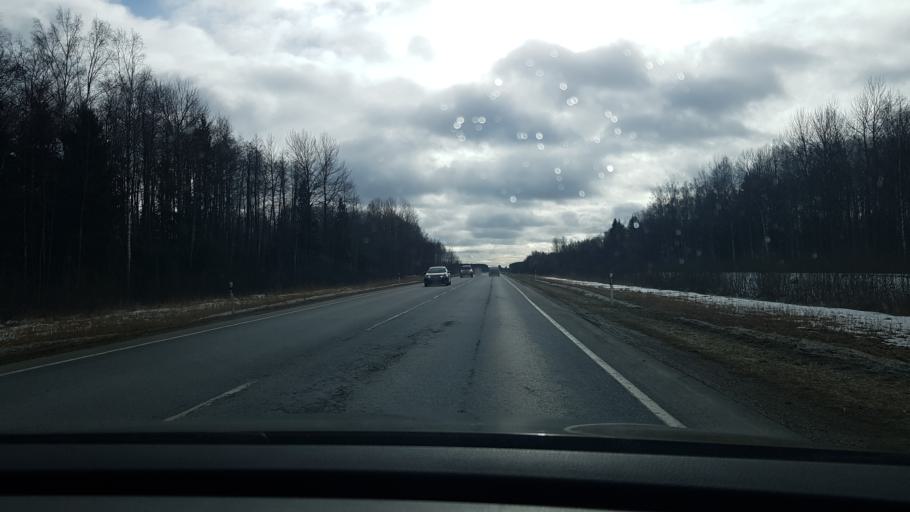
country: EE
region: Paernumaa
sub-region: Sindi linn
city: Sindi
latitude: 58.4541
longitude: 24.6946
